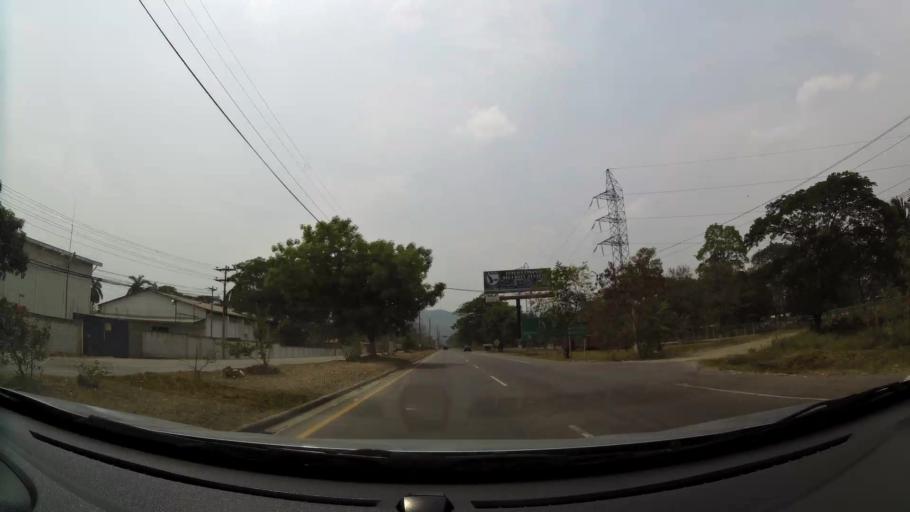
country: HN
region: Cortes
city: Chotepe
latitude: 15.4016
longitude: -88.0014
